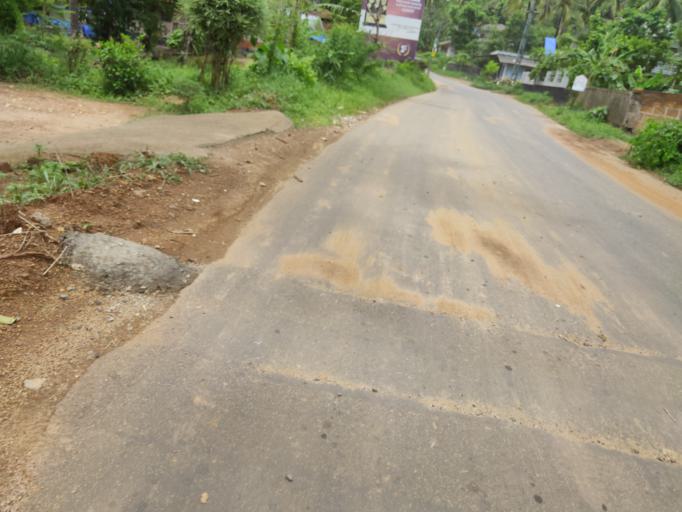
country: IN
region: Kerala
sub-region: Malappuram
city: Manjeri
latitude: 11.2035
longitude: 76.2597
